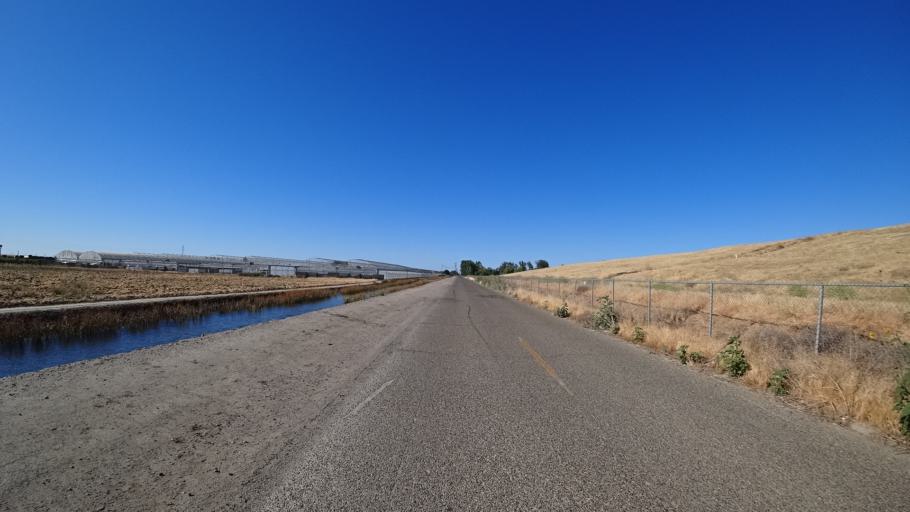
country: US
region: California
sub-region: Fresno County
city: West Park
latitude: 36.6967
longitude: -119.8269
